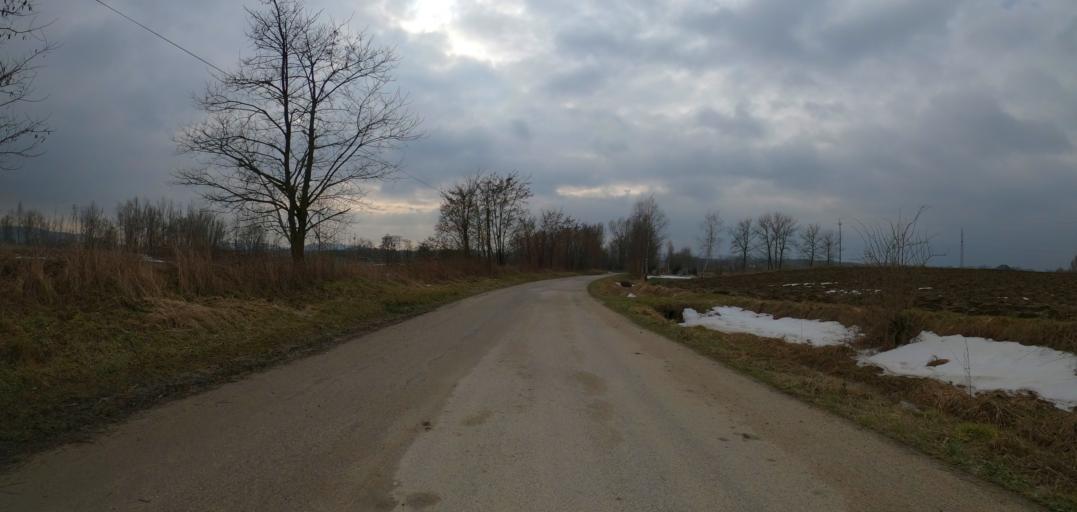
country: PL
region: Subcarpathian Voivodeship
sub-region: Powiat debicki
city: Pilzno
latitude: 49.9748
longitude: 21.3214
